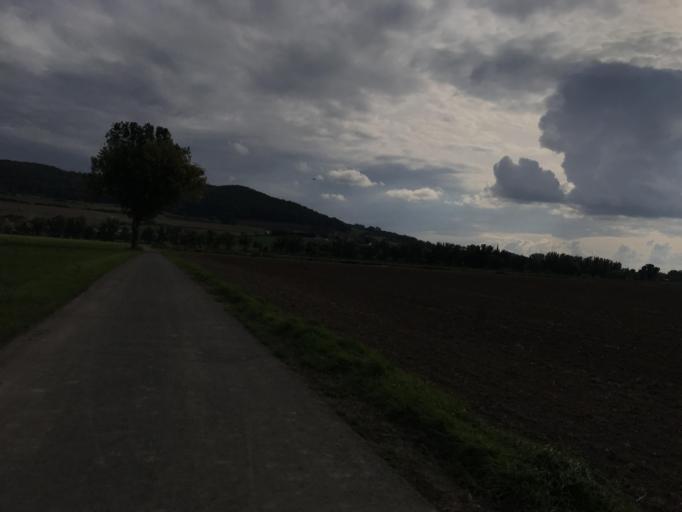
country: DE
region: Hesse
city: Felsberg
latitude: 51.1110
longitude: 9.3916
